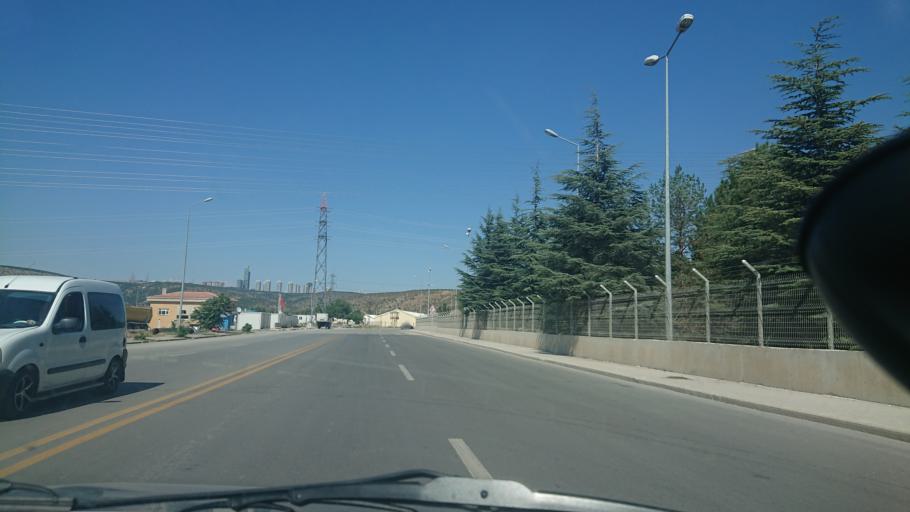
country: TR
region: Ankara
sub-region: Goelbasi
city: Golbasi
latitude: 39.8062
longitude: 32.8152
